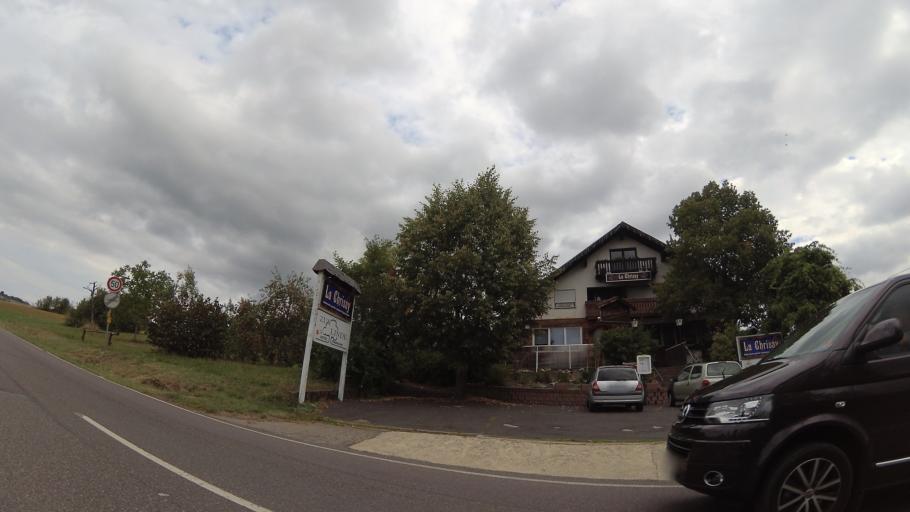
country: DE
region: Saarland
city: Kleinblittersdorf
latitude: 49.1583
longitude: 7.0901
